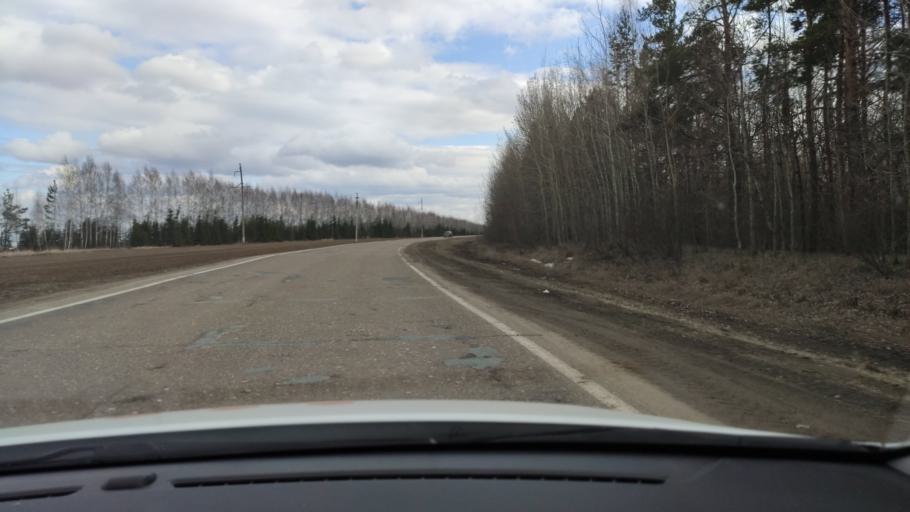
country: RU
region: Tatarstan
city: Vysokaya Gora
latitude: 56.0627
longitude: 49.2036
